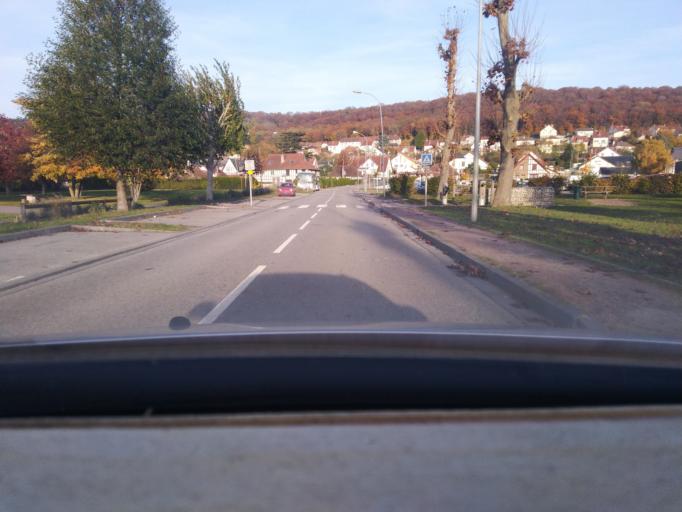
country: FR
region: Haute-Normandie
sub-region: Departement de la Seine-Maritime
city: Le Trait
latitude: 49.4826
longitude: 0.8051
